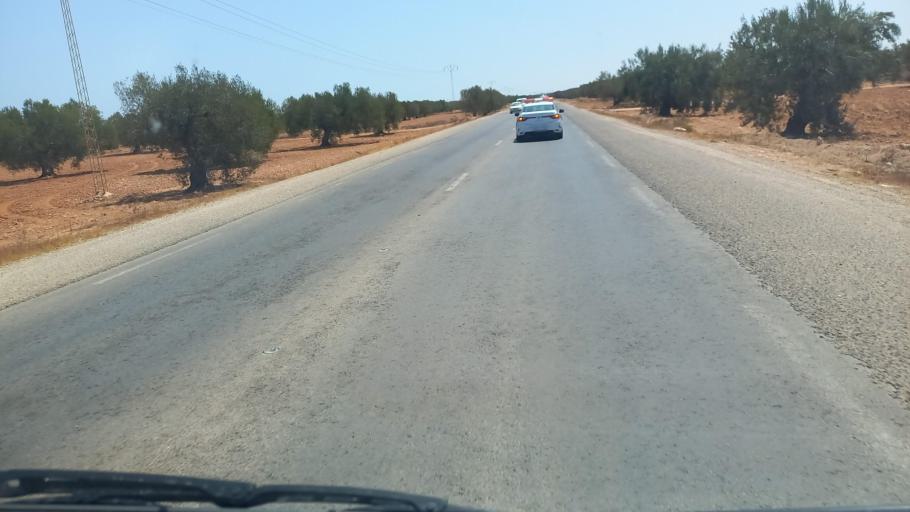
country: TN
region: Madanin
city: Zarzis
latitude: 33.5723
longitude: 11.0409
